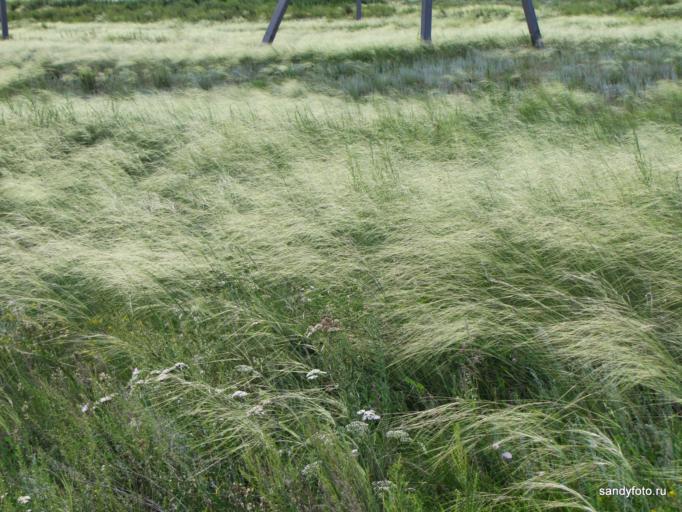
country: RU
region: Chelyabinsk
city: Troitsk
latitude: 54.1002
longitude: 61.5387
